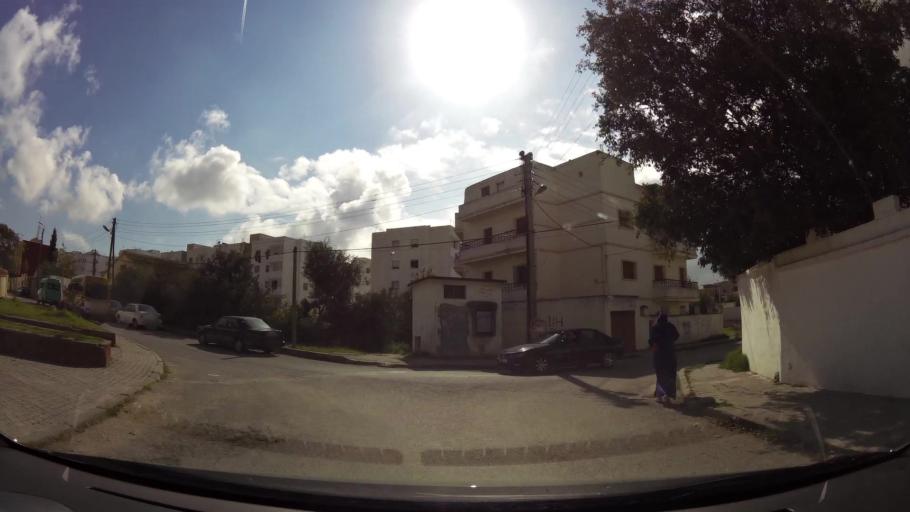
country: MA
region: Tanger-Tetouan
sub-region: Tanger-Assilah
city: Tangier
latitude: 35.7615
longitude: -5.8074
